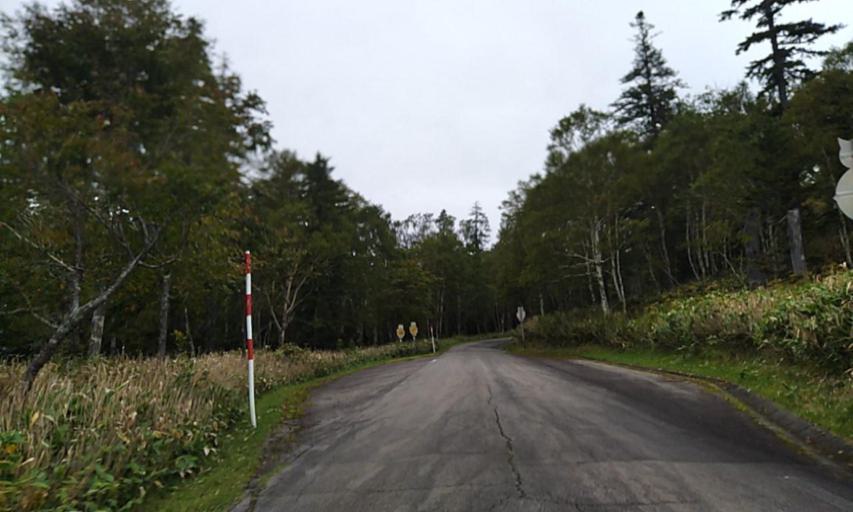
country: JP
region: Hokkaido
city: Bihoro
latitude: 43.5668
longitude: 144.2180
